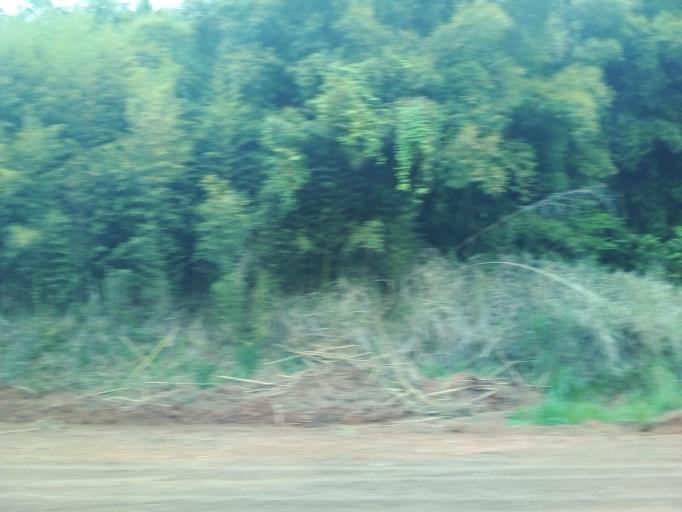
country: BR
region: Minas Gerais
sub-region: Rio Piracicaba
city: Rio Piracicaba
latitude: -19.8712
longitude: -43.1221
